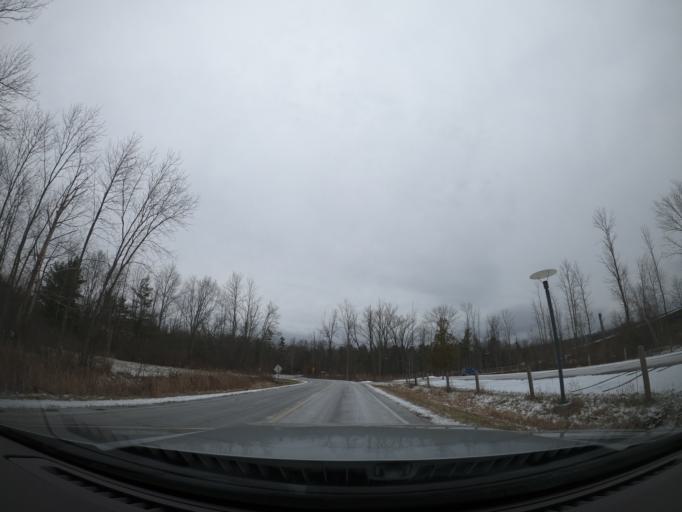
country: US
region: New York
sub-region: Tompkins County
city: Northeast Ithaca
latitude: 42.4810
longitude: -76.4493
